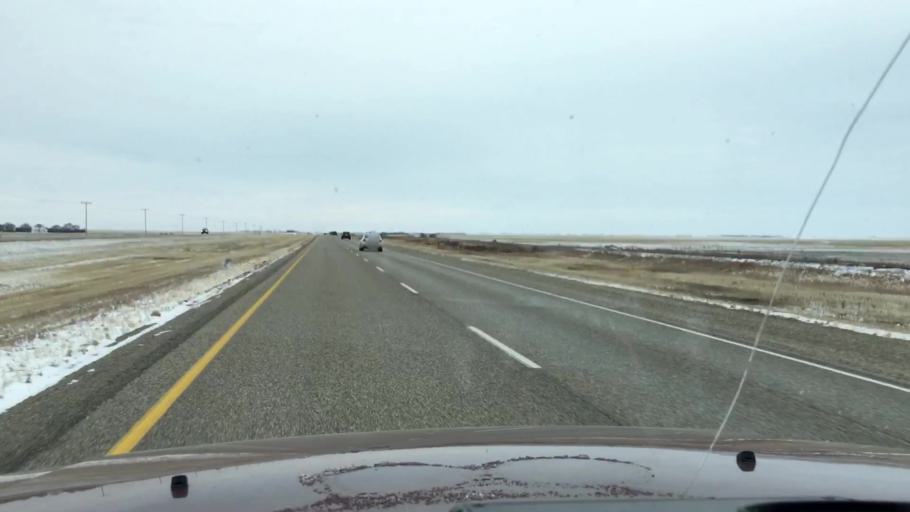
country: CA
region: Saskatchewan
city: Watrous
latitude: 51.1377
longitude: -105.9005
